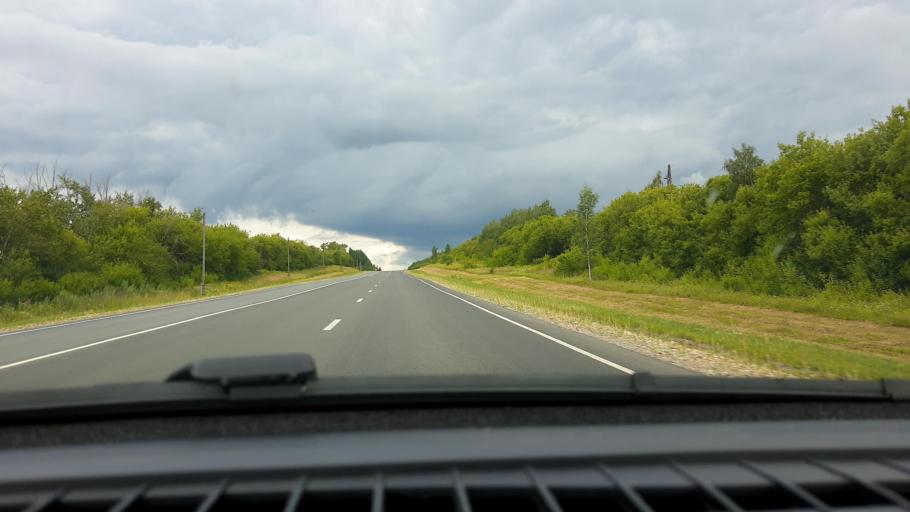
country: RU
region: Nizjnij Novgorod
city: Bol'shoye Murashkino
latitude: 55.8070
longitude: 44.7623
